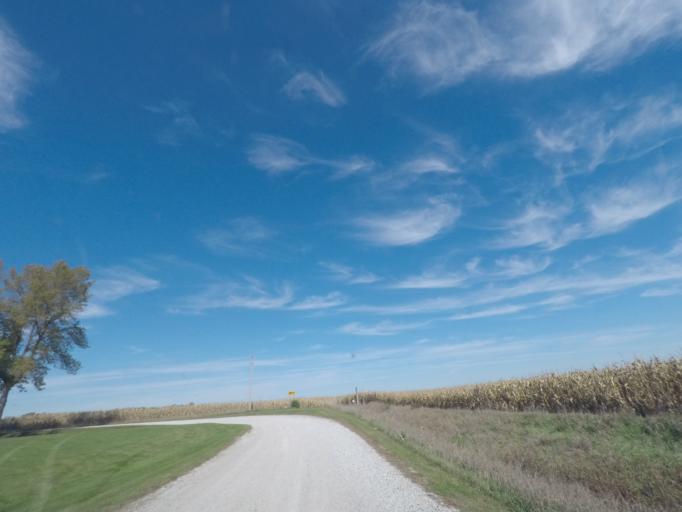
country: US
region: Iowa
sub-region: Story County
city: Nevada
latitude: 42.0116
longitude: -93.3476
